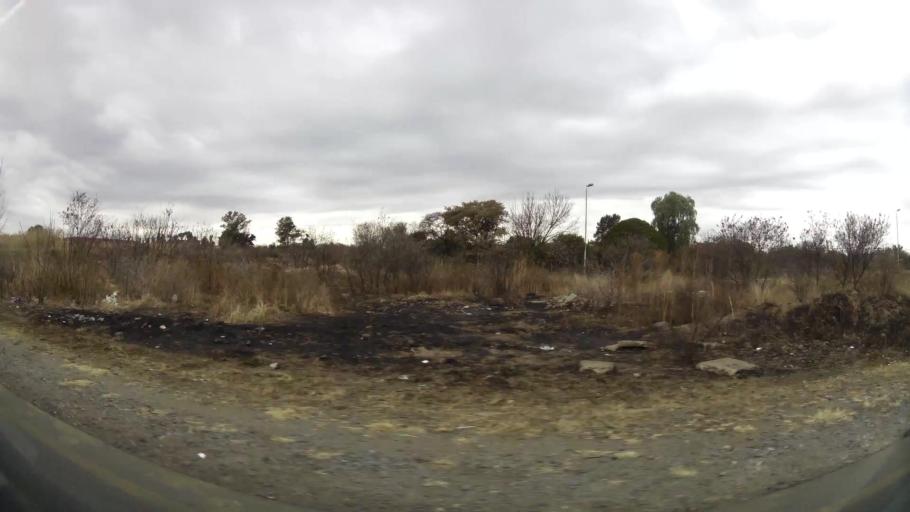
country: ZA
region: Orange Free State
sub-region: Fezile Dabi District Municipality
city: Kroonstad
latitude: -27.6523
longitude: 27.2267
